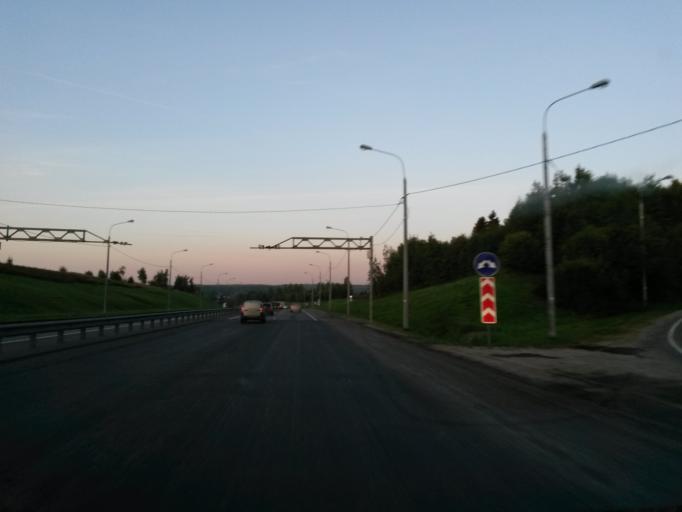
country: RU
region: Moskovskaya
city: Sergiyev Posad
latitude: 56.2874
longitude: 38.2117
